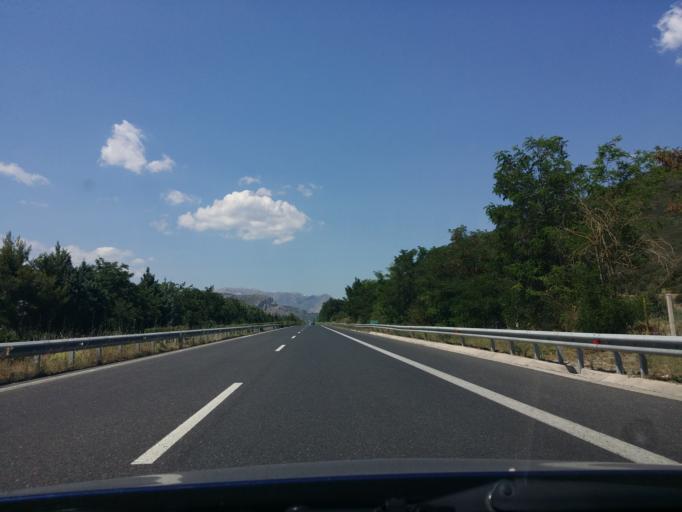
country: GR
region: Peloponnese
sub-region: Nomos Arkadias
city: Tripoli
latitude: 37.5613
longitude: 22.4240
